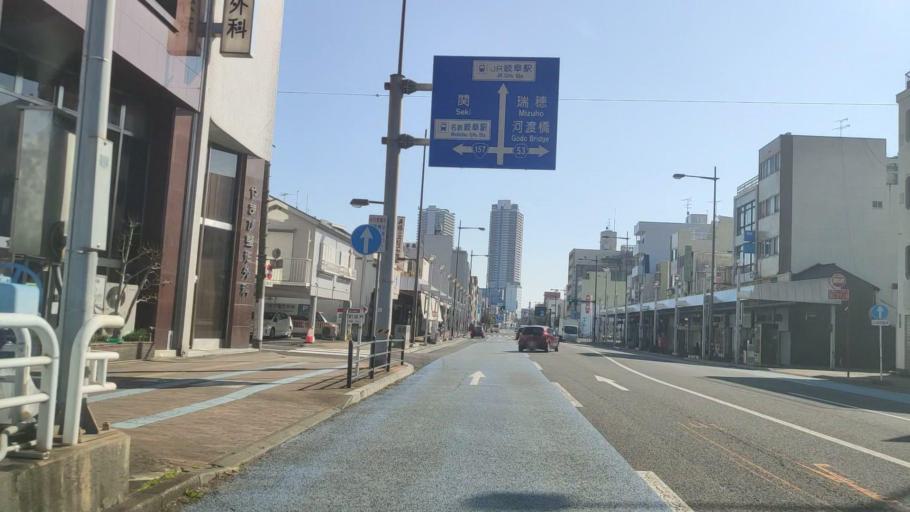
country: JP
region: Gifu
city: Gifu-shi
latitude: 35.4186
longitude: 136.7528
